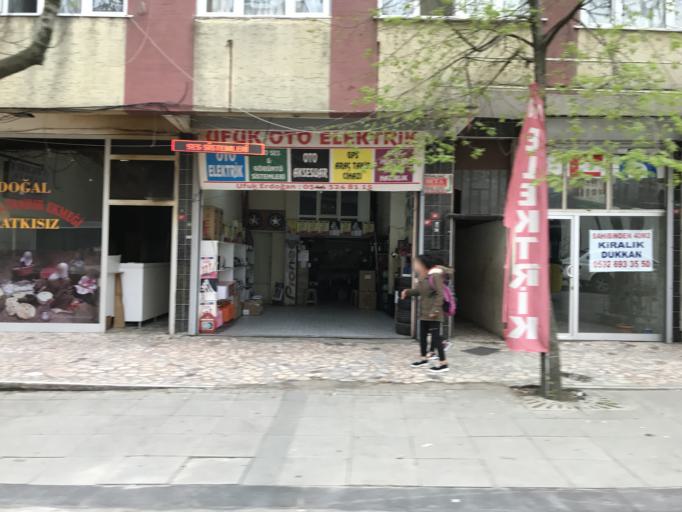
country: TR
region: Istanbul
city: Umraniye
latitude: 41.0118
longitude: 29.1686
